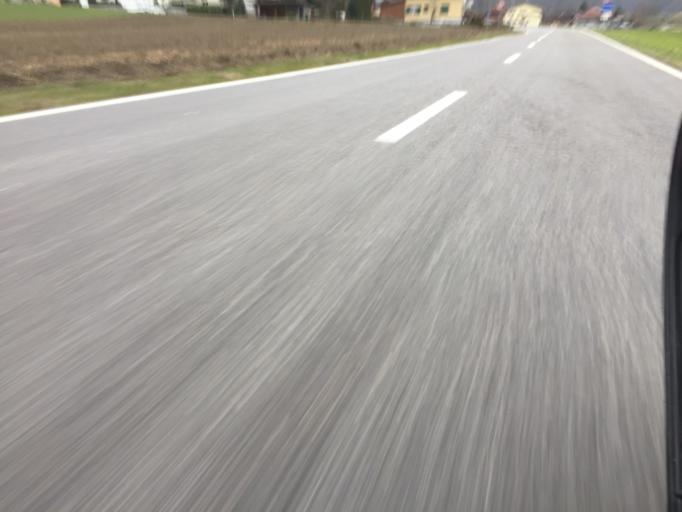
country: CH
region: Bern
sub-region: Emmental District
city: Krauchthal
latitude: 47.0144
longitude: 7.5684
